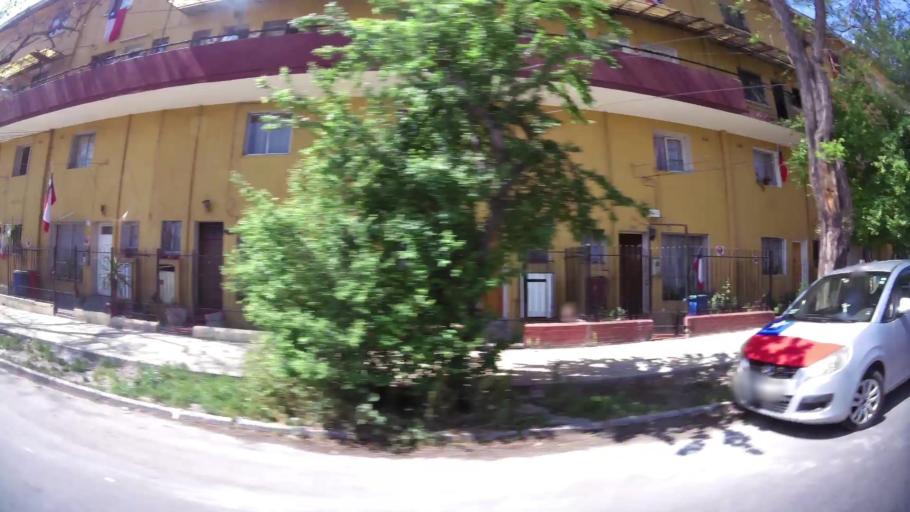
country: CL
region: Santiago Metropolitan
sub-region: Provincia de Santiago
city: Santiago
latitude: -33.4233
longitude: -70.6694
